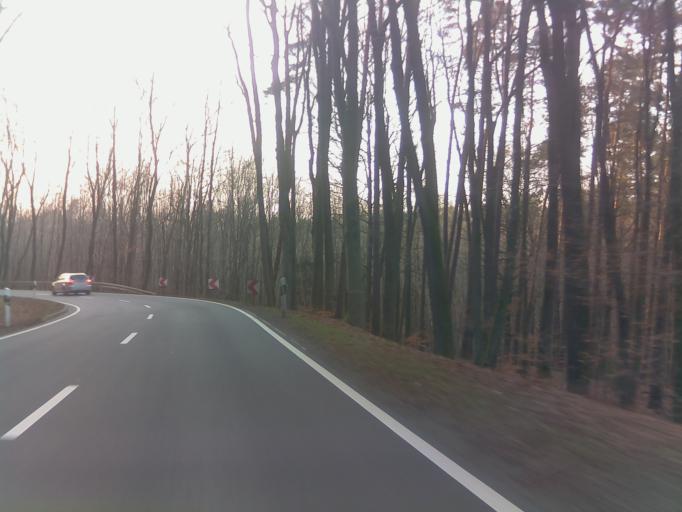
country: DE
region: Hesse
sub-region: Regierungsbezirk Darmstadt
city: Frankisch-Crumbach
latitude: 49.7141
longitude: 8.9074
